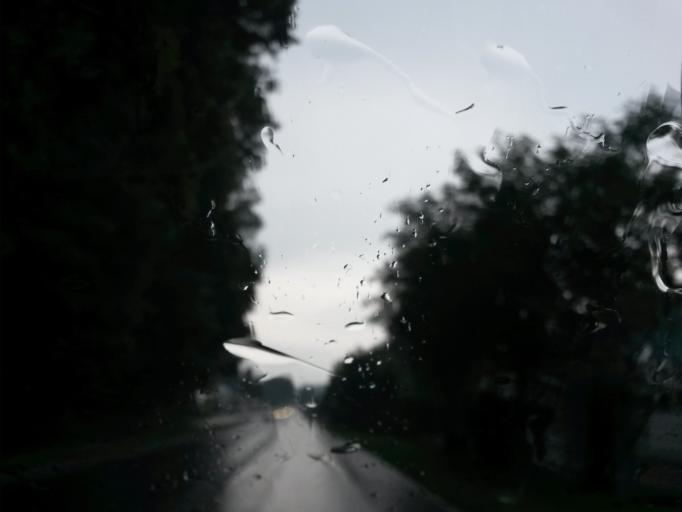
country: DE
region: North Rhine-Westphalia
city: Wiehl
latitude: 50.9855
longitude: 7.5133
